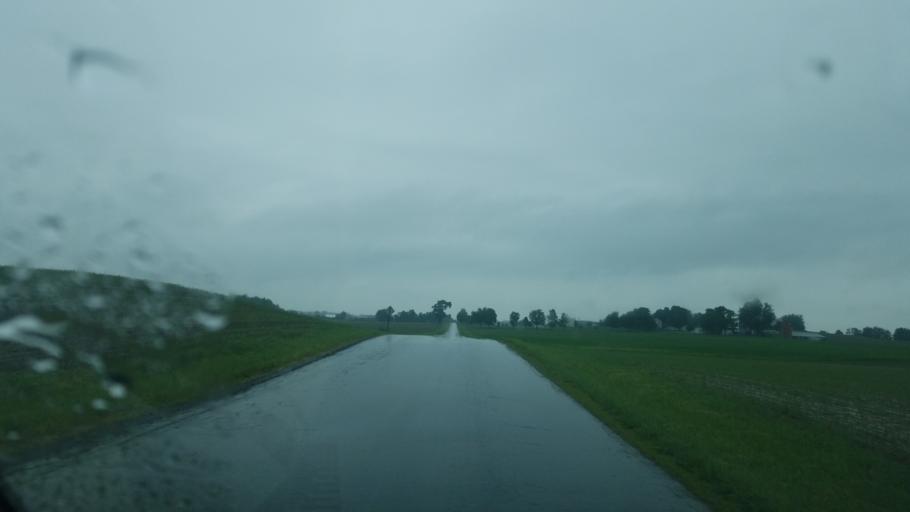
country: US
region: Ohio
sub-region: Huron County
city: Plymouth
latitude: 40.9818
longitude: -82.6059
